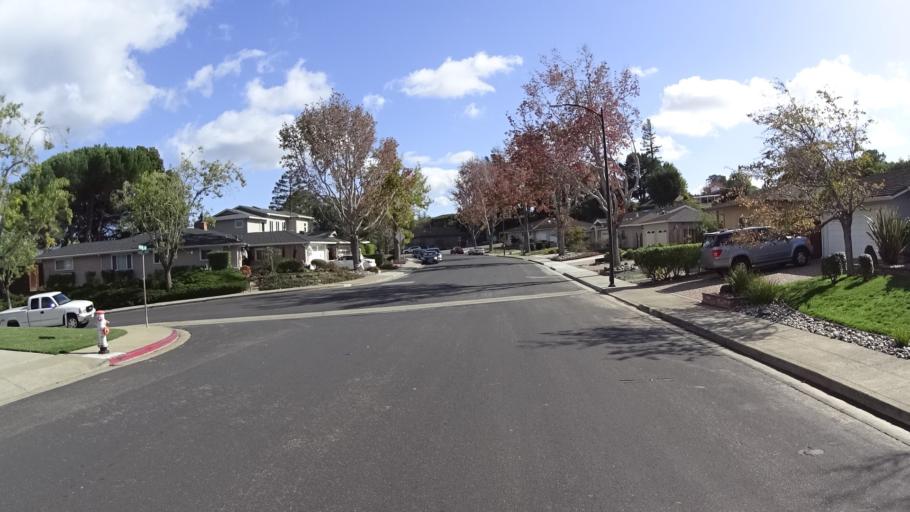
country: US
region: California
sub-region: San Mateo County
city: Millbrae
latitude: 37.5883
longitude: -122.3908
